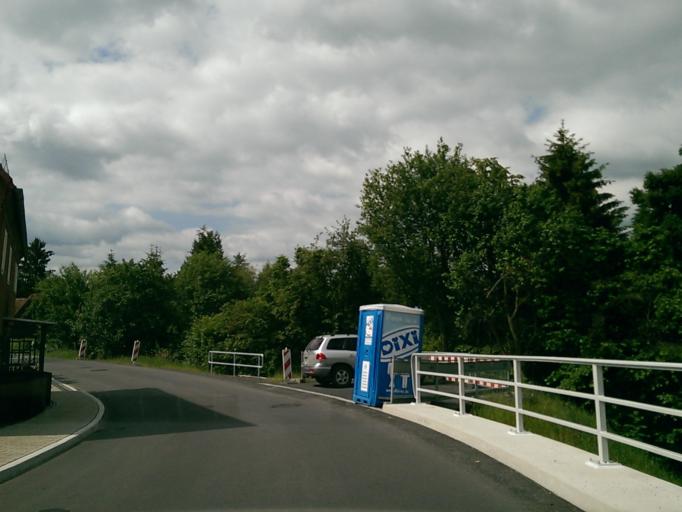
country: DE
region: Saxony
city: Mittelherwigsdorf
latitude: 50.9215
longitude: 14.7667
